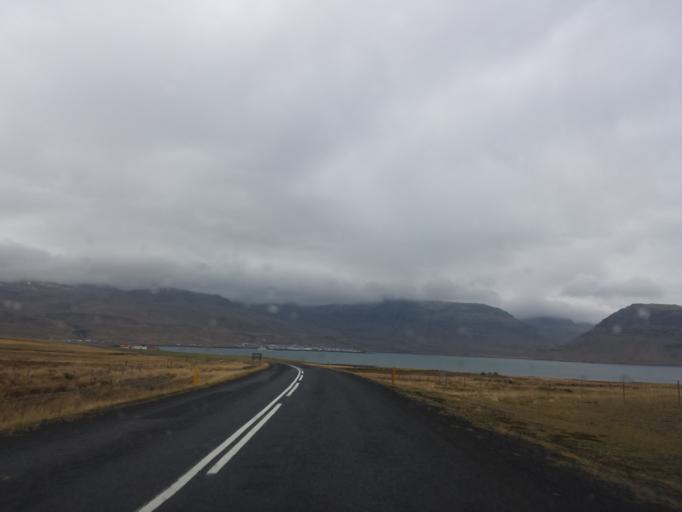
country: IS
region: West
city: Stykkisholmur
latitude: 64.9441
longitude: -23.1924
